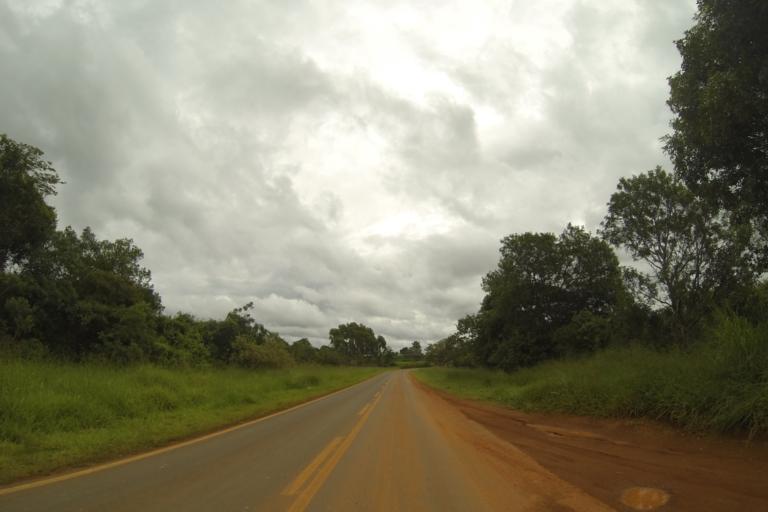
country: BR
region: Minas Gerais
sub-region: Bambui
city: Bambui
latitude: -20.0240
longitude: -46.1923
